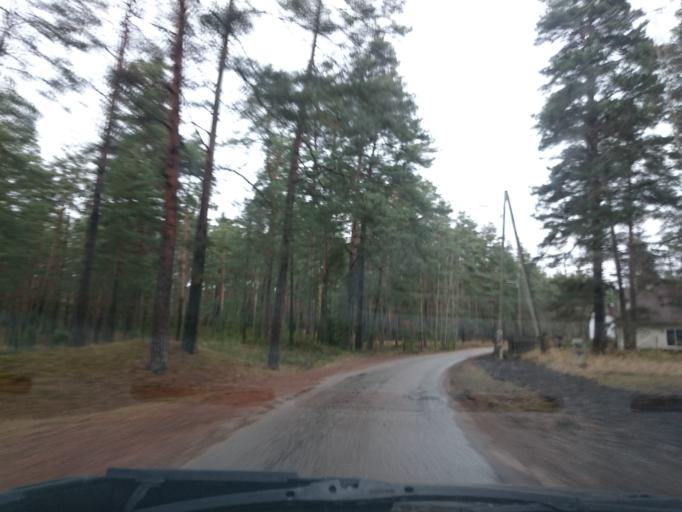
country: LV
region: Riga
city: Bergi
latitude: 57.0144
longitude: 24.3356
